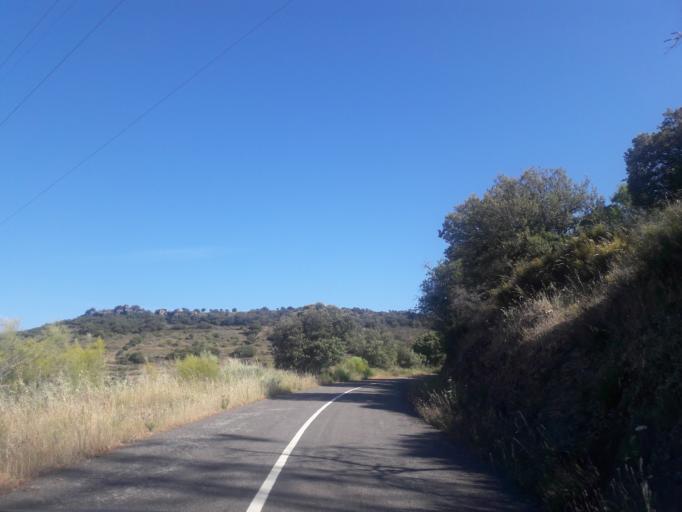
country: ES
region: Castille and Leon
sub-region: Provincia de Salamanca
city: Saucelle
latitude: 41.0332
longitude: -6.7703
